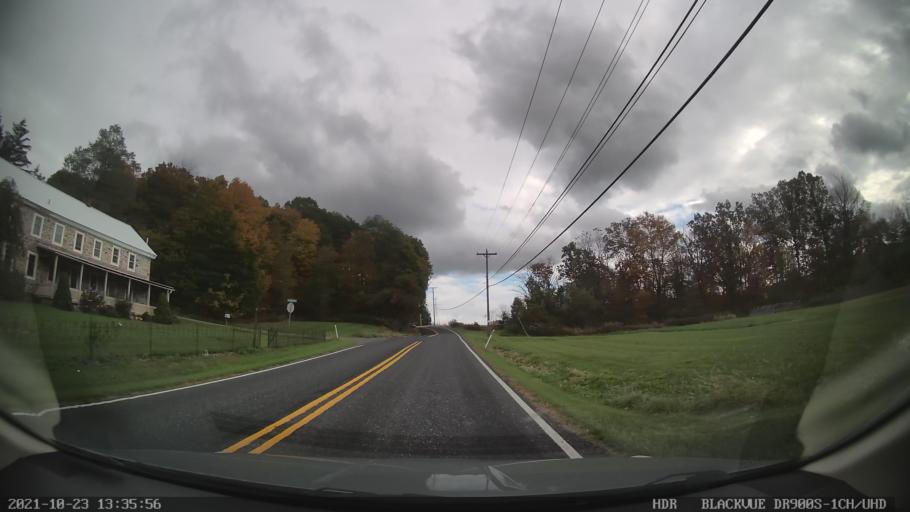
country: US
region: Pennsylvania
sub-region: Berks County
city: Red Lion
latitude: 40.4436
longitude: -75.6147
